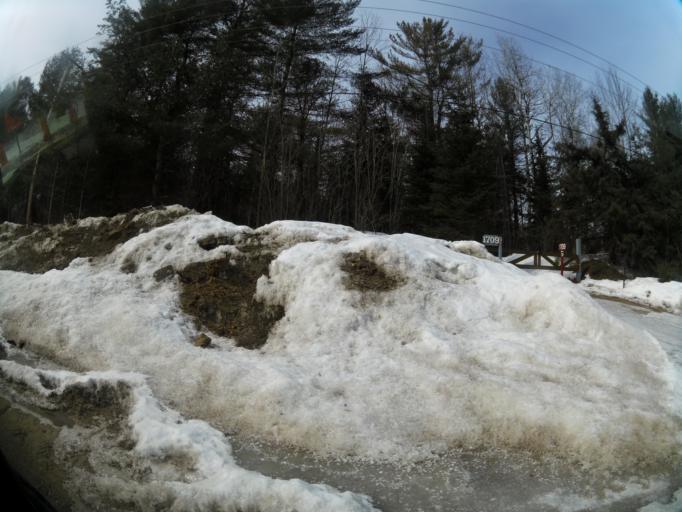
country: CA
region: Quebec
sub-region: Outaouais
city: Val-des-Monts
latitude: 45.9743
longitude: -75.5573
